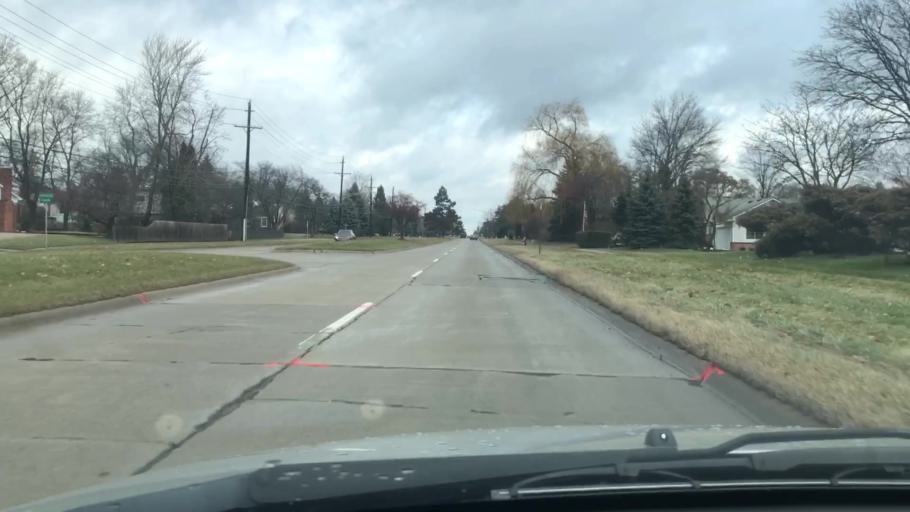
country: US
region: Michigan
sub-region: Oakland County
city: Birmingham
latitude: 42.5699
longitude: -83.1873
